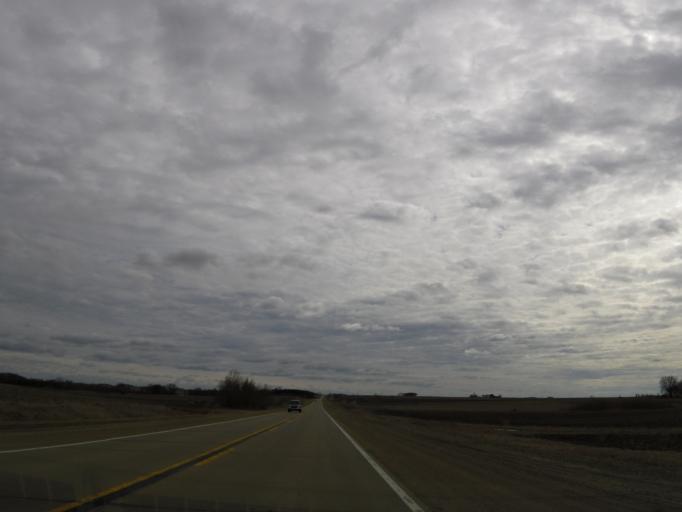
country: US
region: Iowa
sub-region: Howard County
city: Cresco
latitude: 43.3990
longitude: -92.2984
